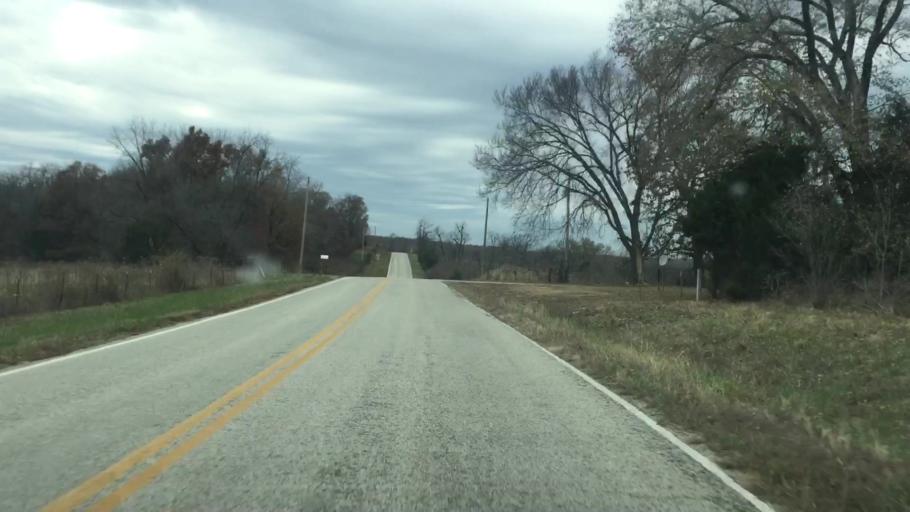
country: US
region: Missouri
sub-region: Saint Clair County
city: Osceola
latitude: 37.9890
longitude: -93.6144
